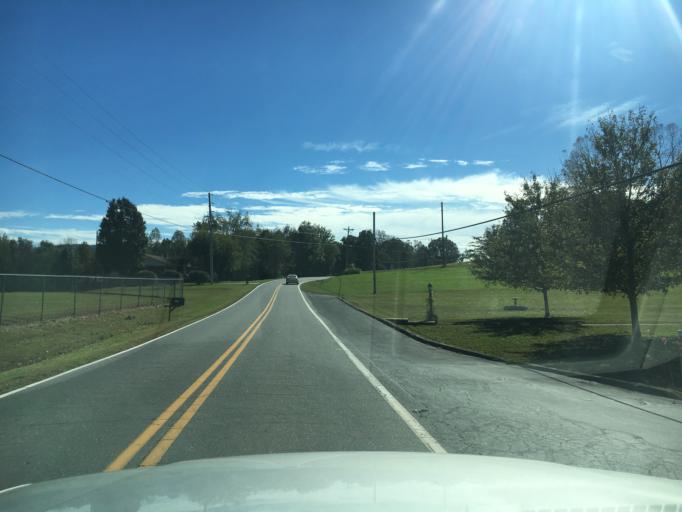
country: US
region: North Carolina
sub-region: Burke County
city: Salem
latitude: 35.7035
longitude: -81.7354
